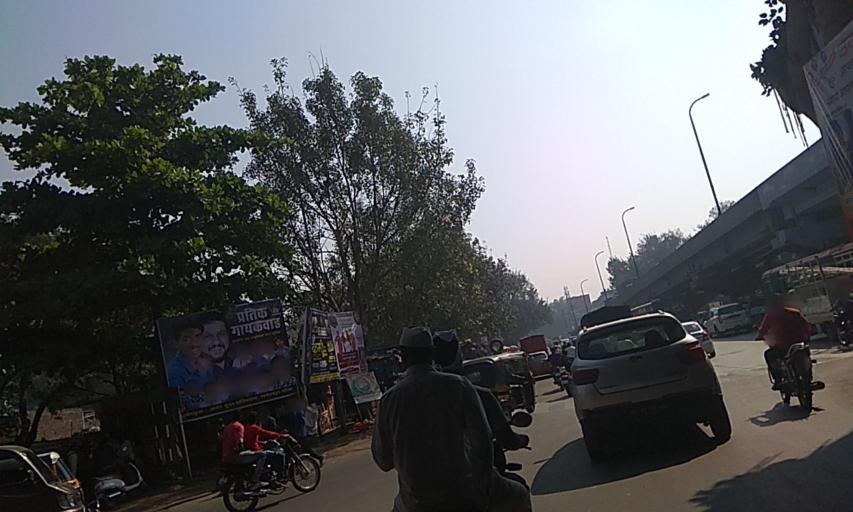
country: IN
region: Maharashtra
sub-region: Pune Division
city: Pune
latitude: 18.5026
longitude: 73.9275
